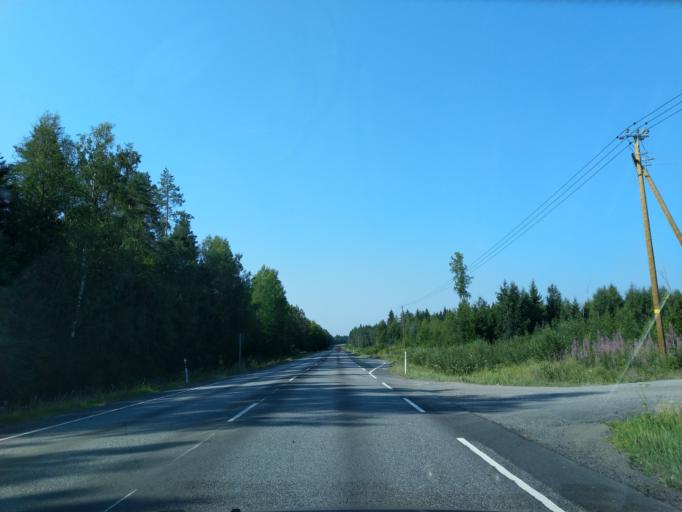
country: FI
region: Satakunta
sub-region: Pori
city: Pomarkku
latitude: 61.7184
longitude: 22.0495
